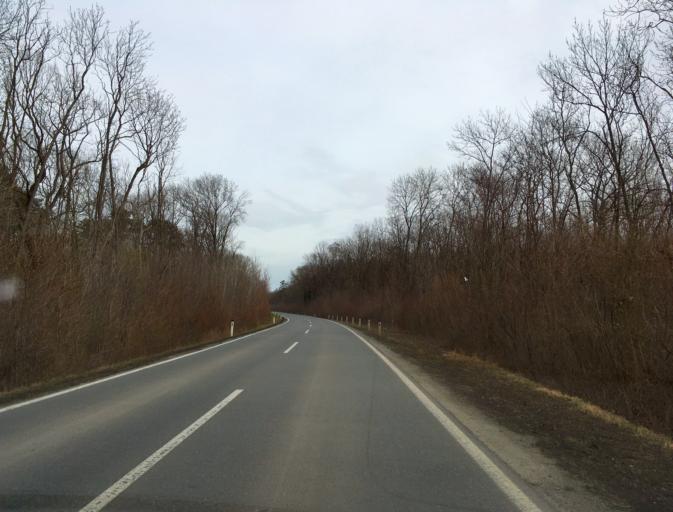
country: AT
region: Lower Austria
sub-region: Politischer Bezirk Ganserndorf
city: Leopoldsdorf im Marchfelde
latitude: 48.2264
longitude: 16.6994
